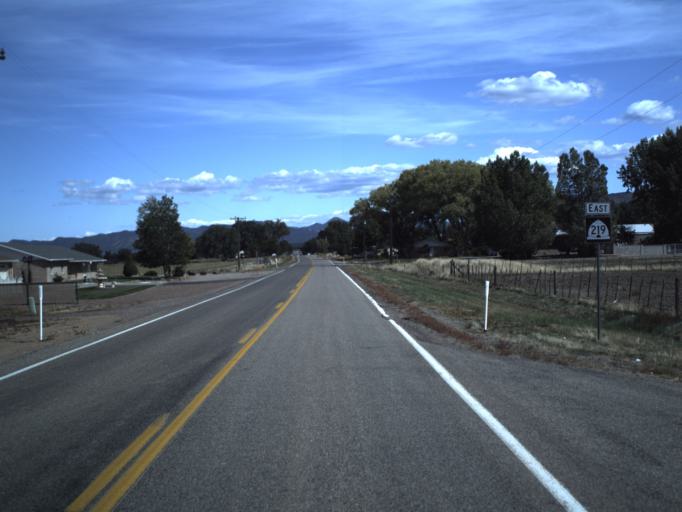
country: US
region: Utah
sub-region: Washington County
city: Enterprise
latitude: 37.5735
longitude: -113.7345
